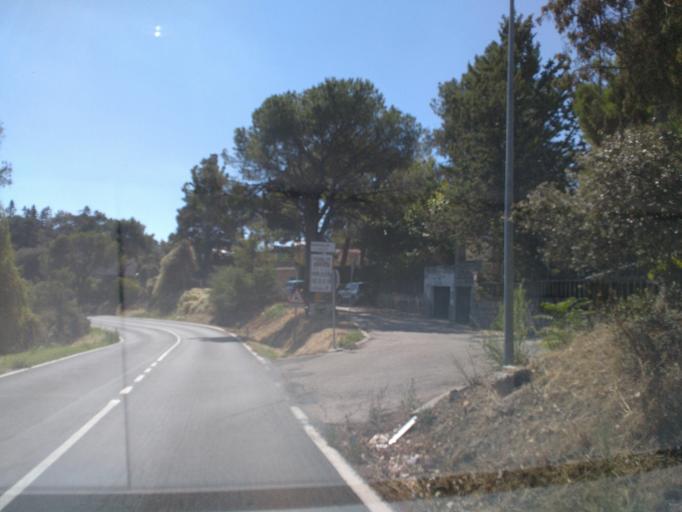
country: ES
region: Madrid
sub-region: Provincia de Madrid
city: Robledo de Chavela
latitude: 40.5173
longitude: -4.2463
